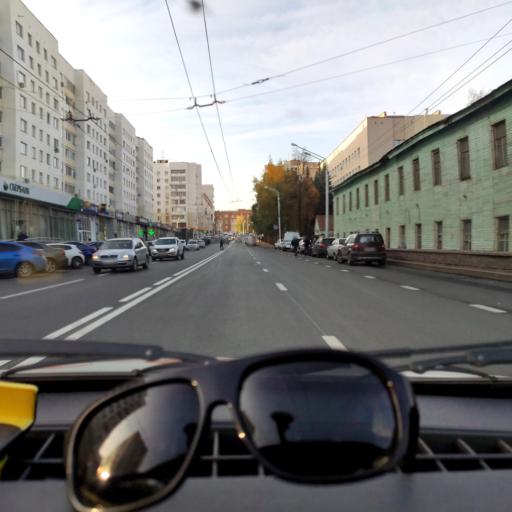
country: RU
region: Bashkortostan
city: Ufa
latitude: 54.7360
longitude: 55.9457
